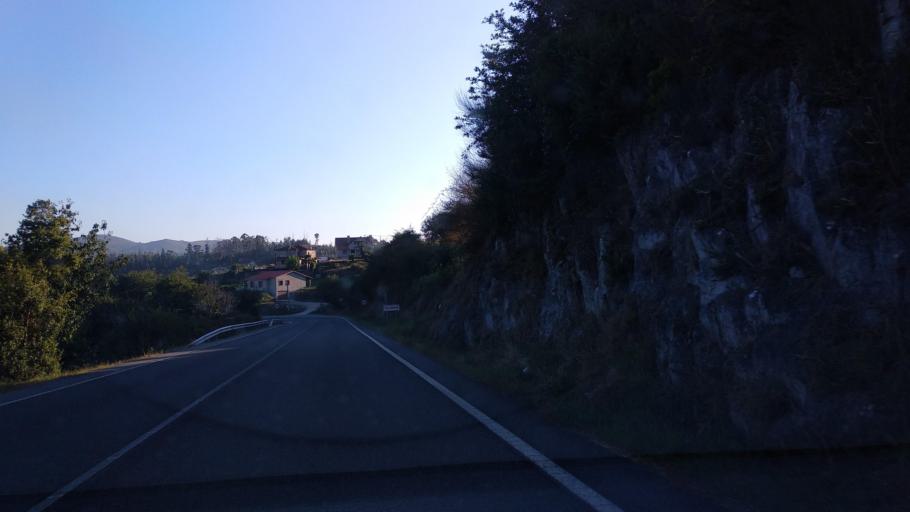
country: ES
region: Galicia
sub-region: Provincia de Pontevedra
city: Ponte Caldelas
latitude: 42.3567
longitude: -8.5418
